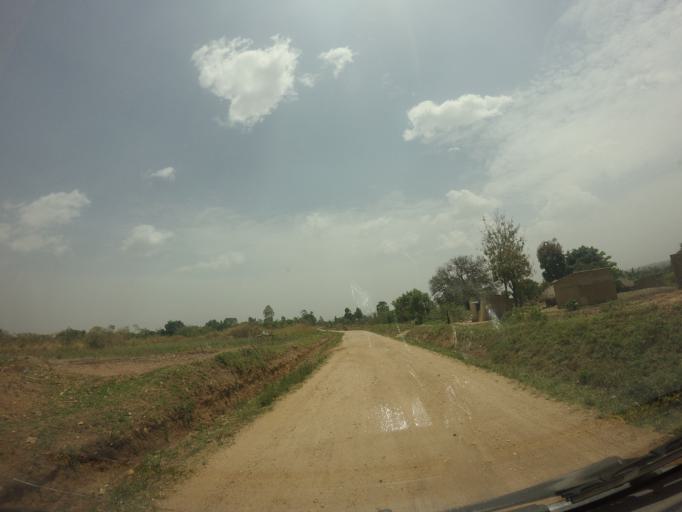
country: UG
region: Northern Region
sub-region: Arua District
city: Arua
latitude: 2.9432
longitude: 30.9134
